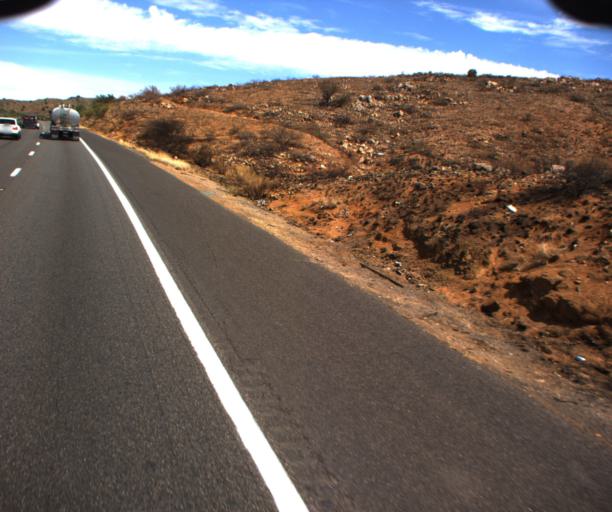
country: US
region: Arizona
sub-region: Yavapai County
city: Cordes Lakes
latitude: 34.2952
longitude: -112.1246
